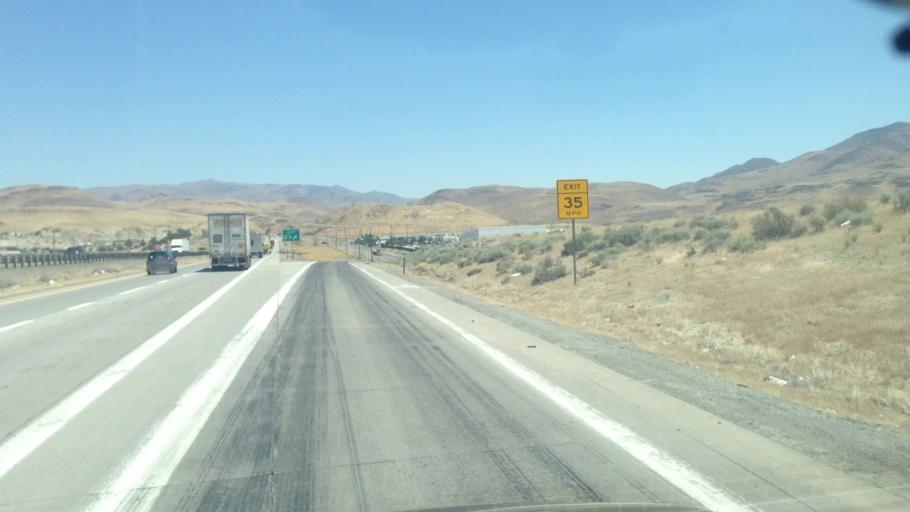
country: US
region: Nevada
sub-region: Washoe County
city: Sparks
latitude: 39.5171
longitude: -119.6325
